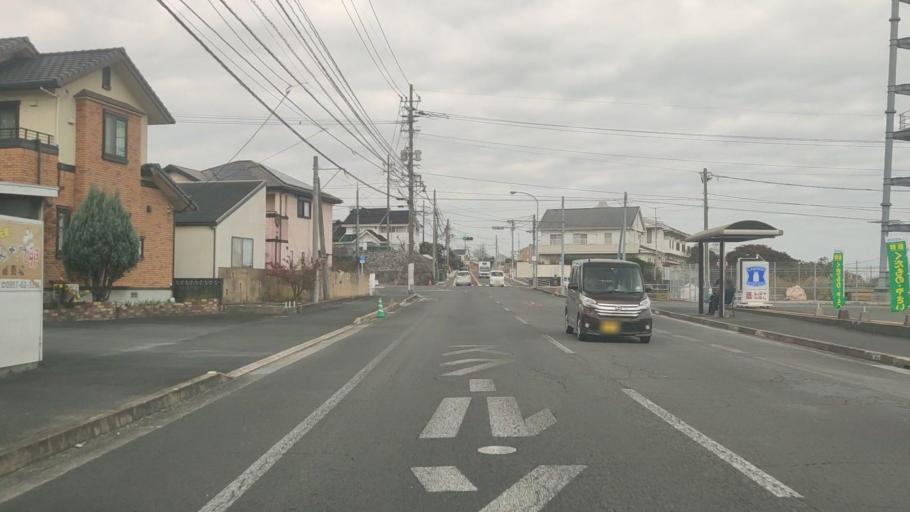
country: JP
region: Nagasaki
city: Shimabara
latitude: 32.8148
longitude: 130.3568
